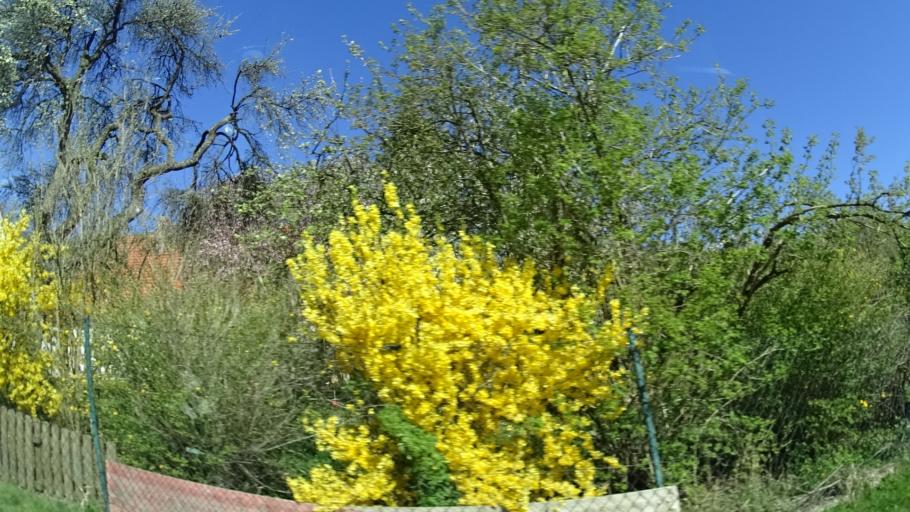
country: DE
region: Bavaria
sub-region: Regierungsbezirk Mittelfranken
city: Alfeld
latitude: 49.4261
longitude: 11.5274
